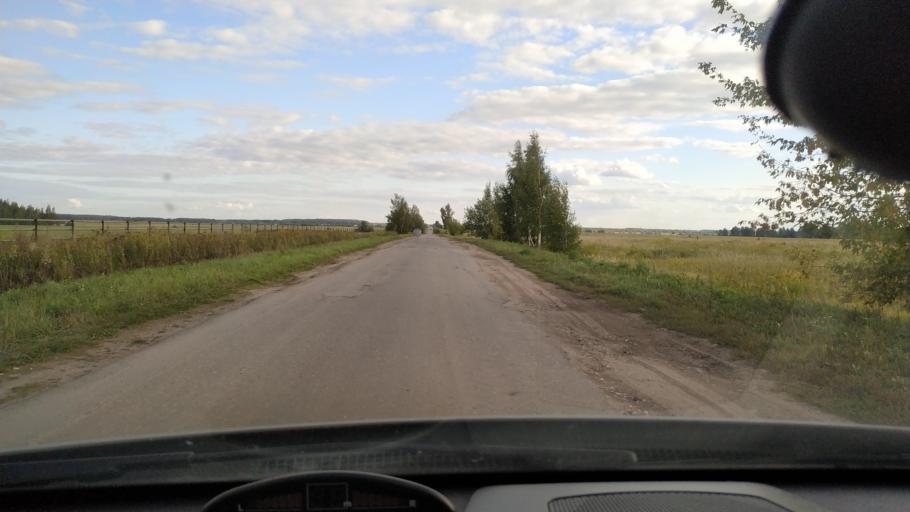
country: RU
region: Rjazan
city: Polyany
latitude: 54.5773
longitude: 39.8608
